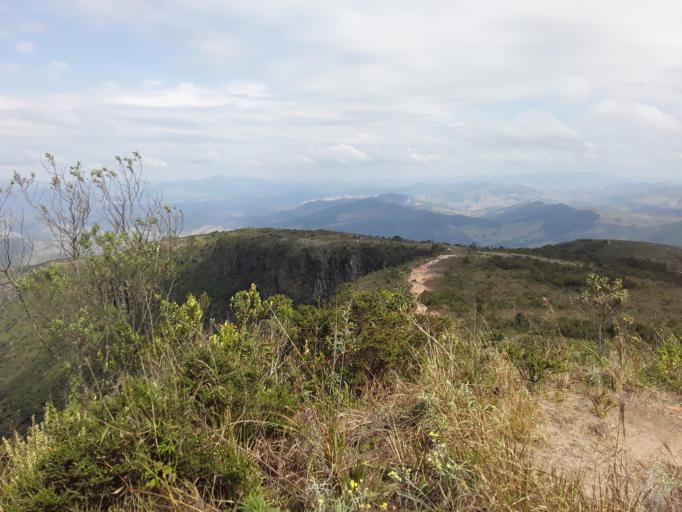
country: BR
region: Minas Gerais
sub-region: Lima Duarte
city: Lima Duarte
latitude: -21.7061
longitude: -43.8713
